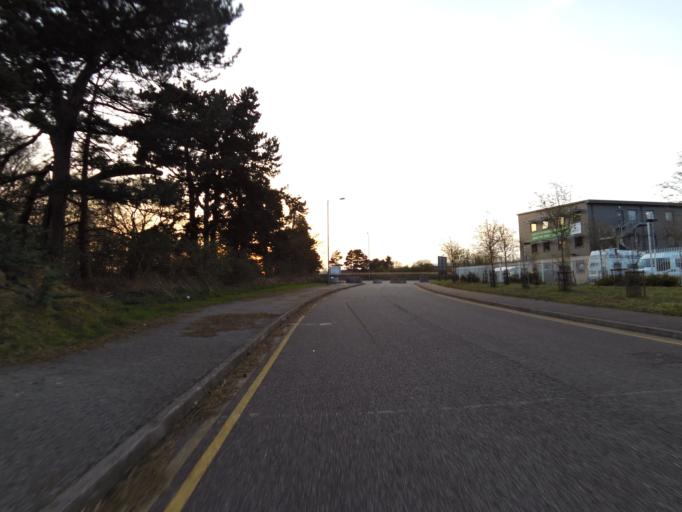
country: GB
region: England
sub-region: Suffolk
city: Kesgrave
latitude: 52.0272
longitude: 1.2203
